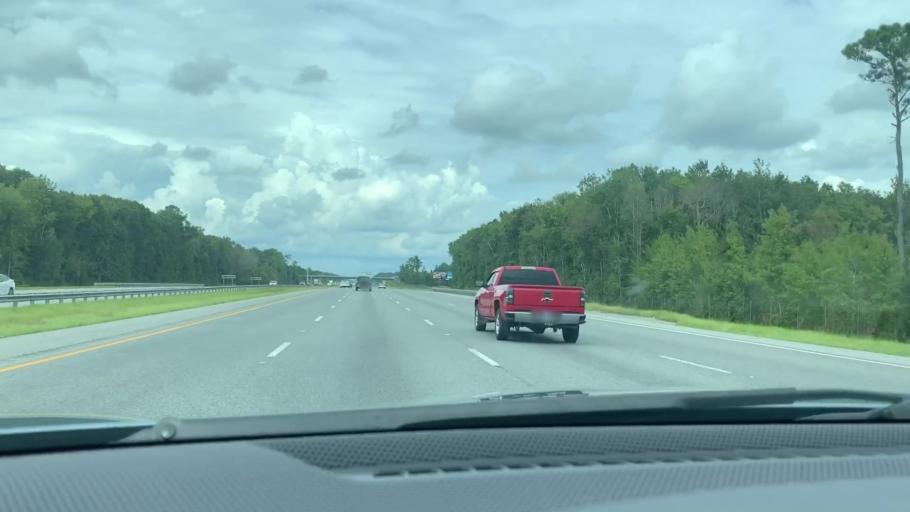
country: US
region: Georgia
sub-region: McIntosh County
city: Darien
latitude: 31.4867
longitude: -81.4469
